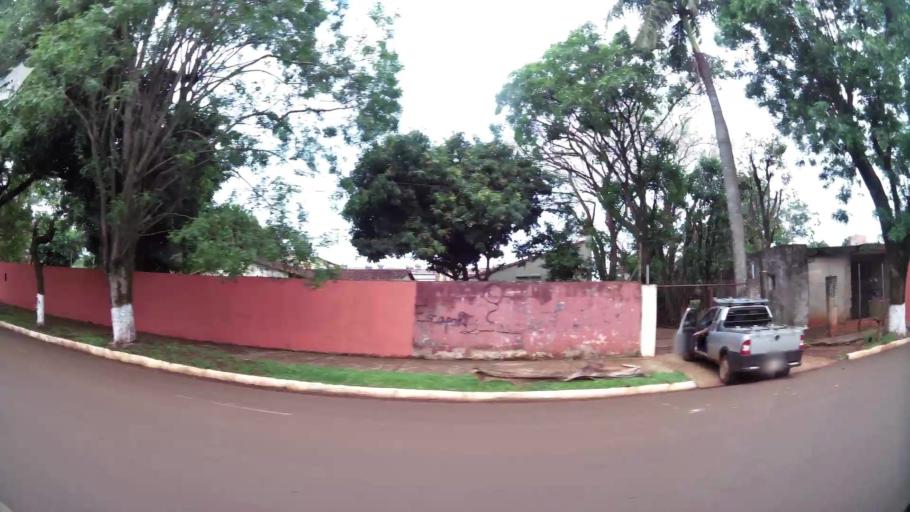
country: PY
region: Alto Parana
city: Ciudad del Este
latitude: -25.4035
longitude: -54.6418
